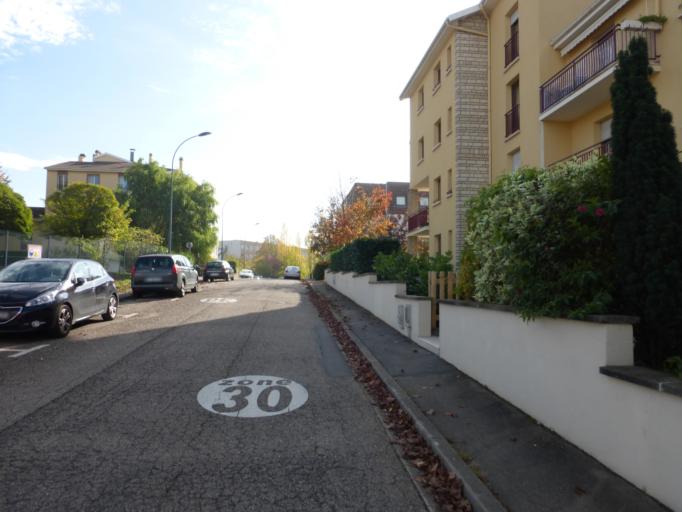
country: FR
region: Lorraine
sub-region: Departement de Meurthe-et-Moselle
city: Villers-les-Nancy
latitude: 48.6747
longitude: 6.1566
